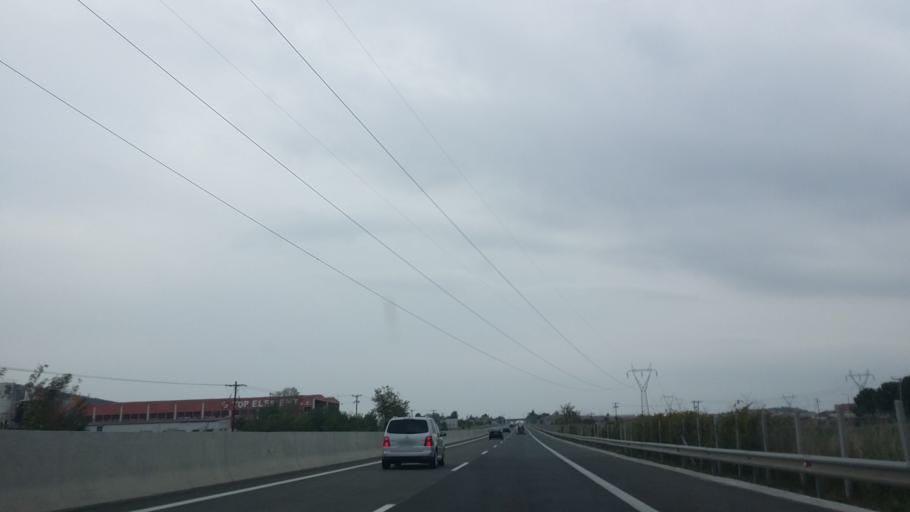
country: GR
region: Central Greece
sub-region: Nomos Voiotias
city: Arma
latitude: 38.3783
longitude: 23.4715
